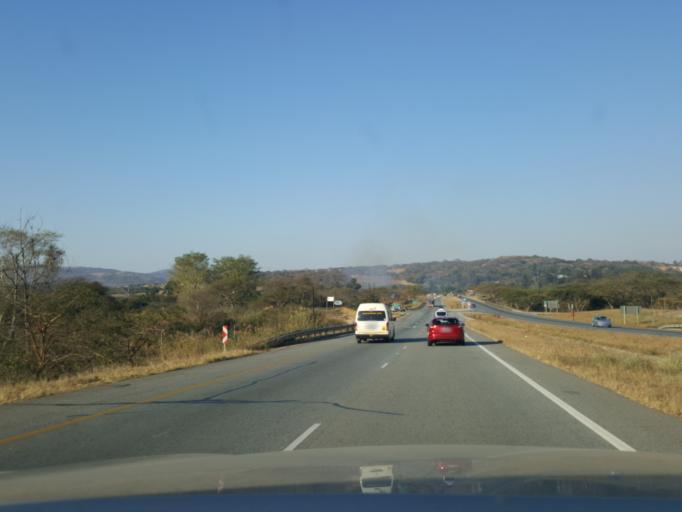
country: ZA
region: Mpumalanga
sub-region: Ehlanzeni District
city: Nelspruit
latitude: -25.4498
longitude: 30.8238
